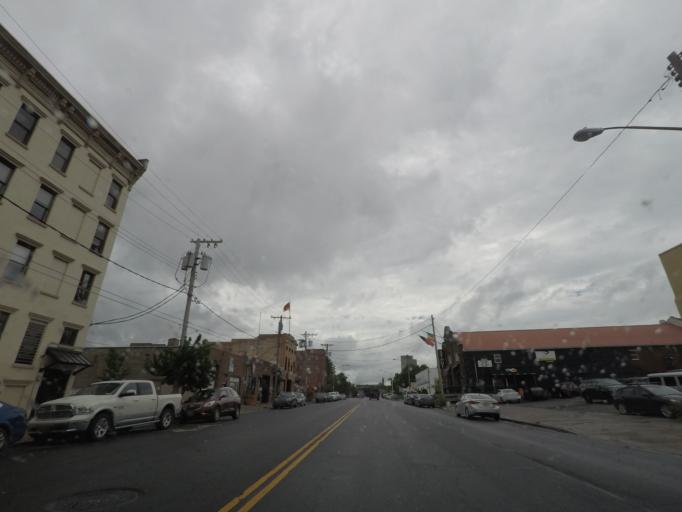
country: US
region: New York
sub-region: Albany County
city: Albany
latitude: 42.6616
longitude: -73.7445
